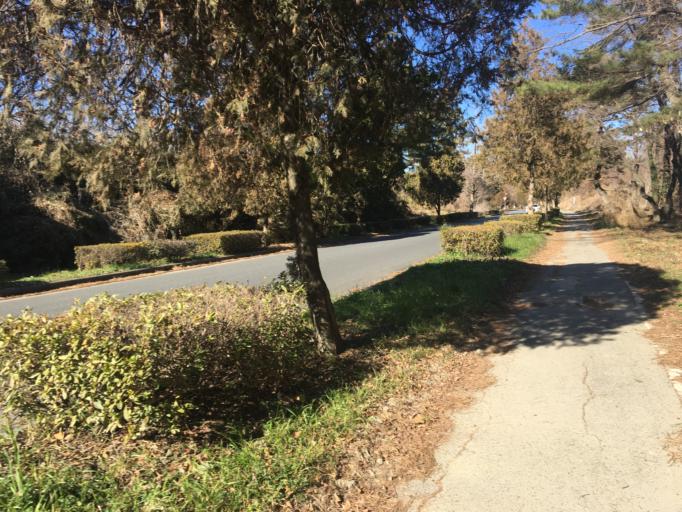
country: JP
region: Saitama
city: Shiki
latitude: 35.8418
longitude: 139.6089
